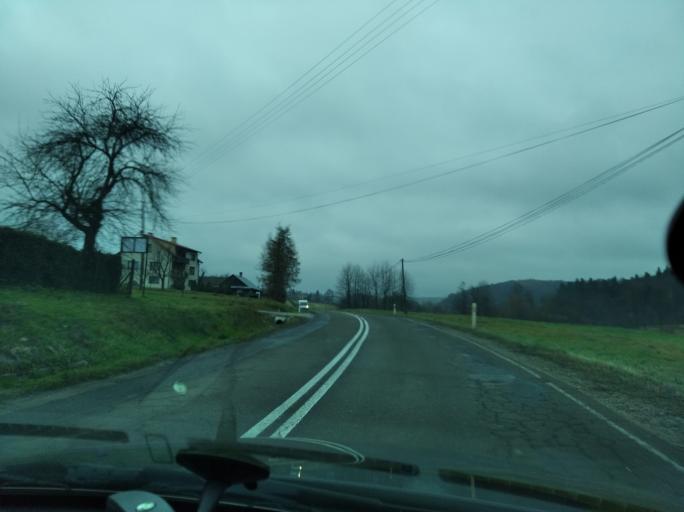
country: PL
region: Subcarpathian Voivodeship
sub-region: Powiat rzeszowski
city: Dynow
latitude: 49.8566
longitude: 22.2502
